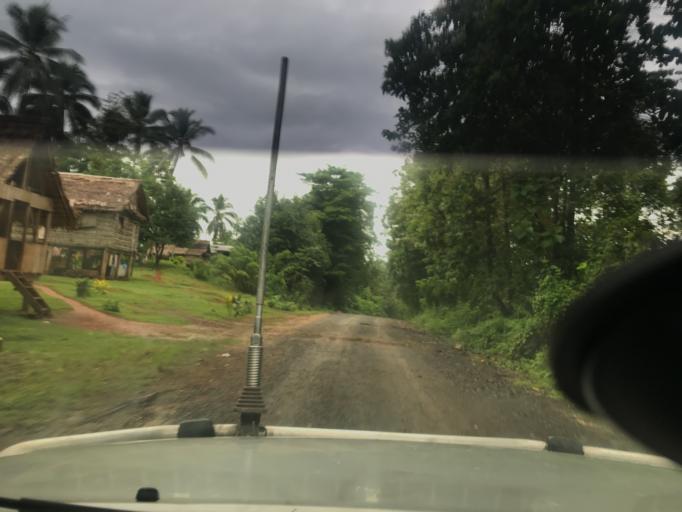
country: SB
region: Malaita
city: Auki
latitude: -8.9492
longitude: 160.7787
